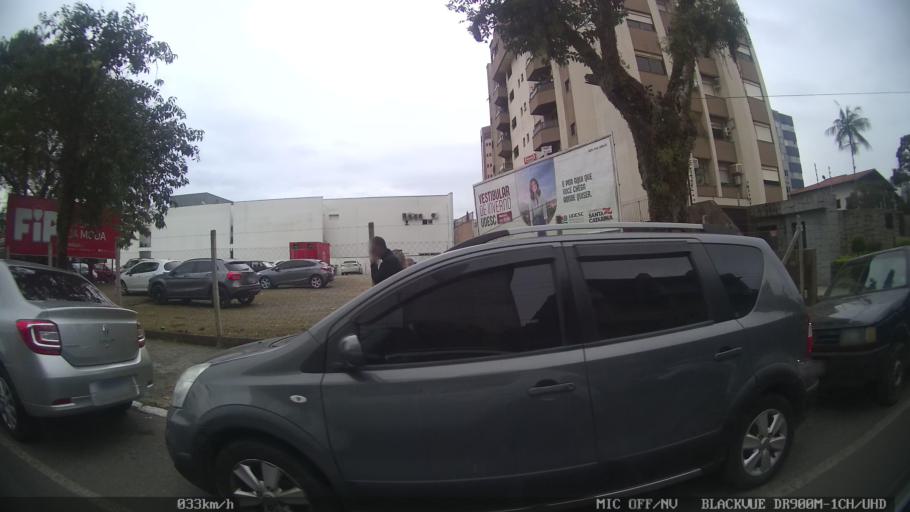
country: BR
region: Santa Catarina
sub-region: Joinville
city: Joinville
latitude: -26.2881
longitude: -48.8453
